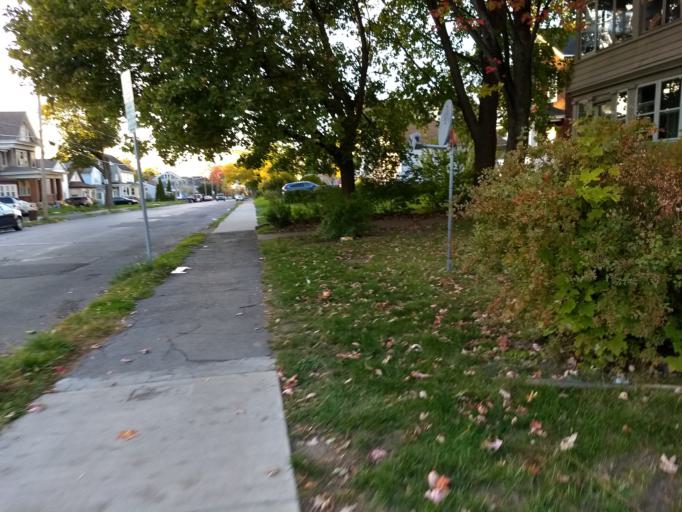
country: US
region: New York
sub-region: Onondaga County
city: Syracuse
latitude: 43.0700
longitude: -76.1504
